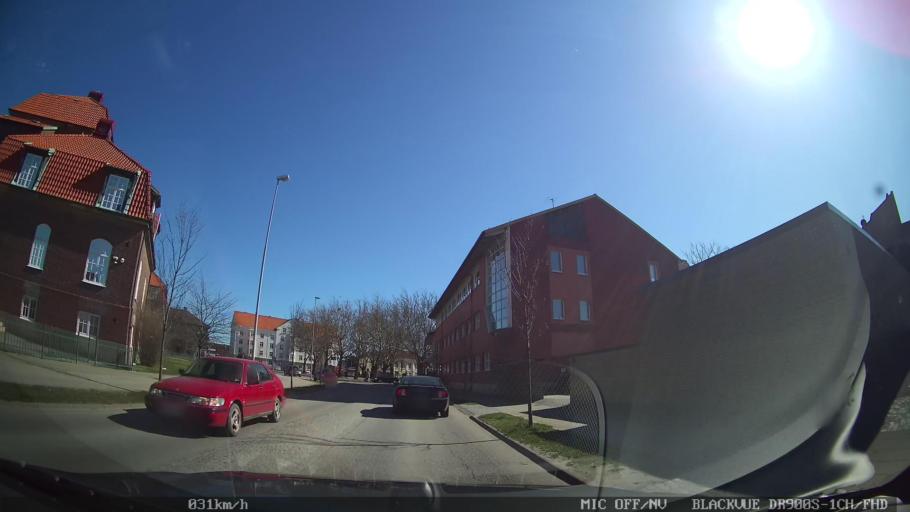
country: SE
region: Skane
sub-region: Ystads Kommun
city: Ystad
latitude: 55.4310
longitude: 13.8265
